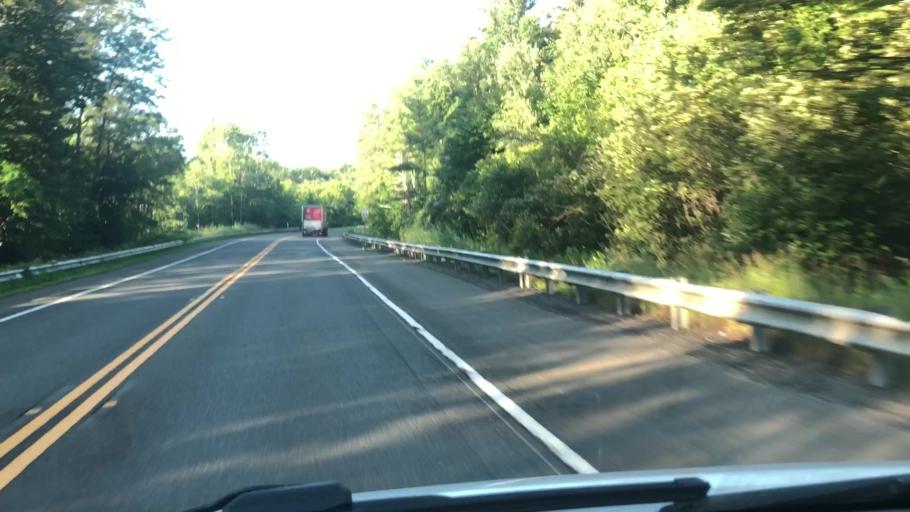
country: US
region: Massachusetts
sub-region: Hampshire County
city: Chesterfield
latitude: 42.4434
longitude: -72.8605
